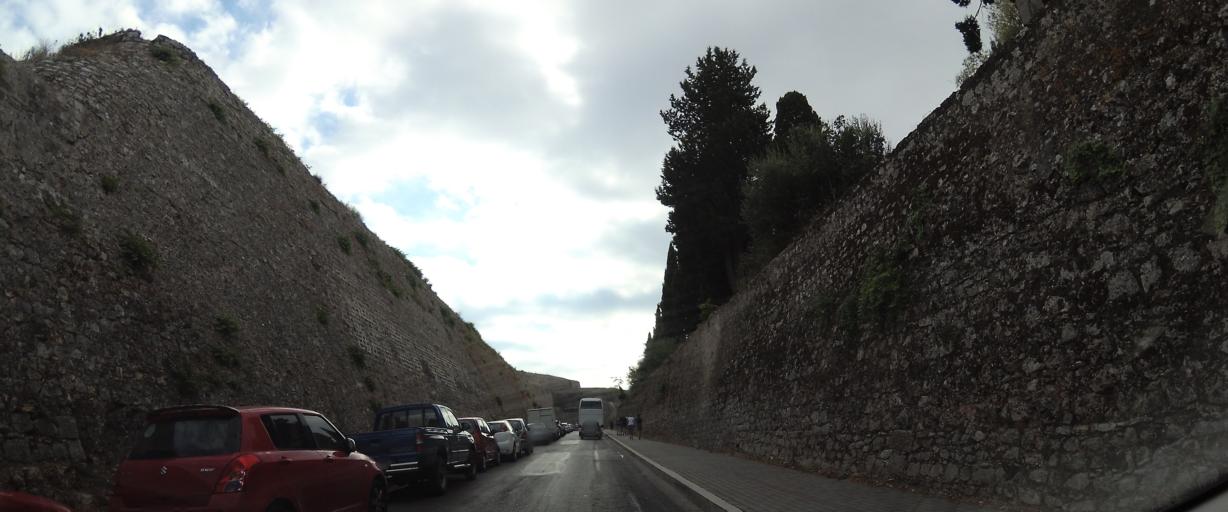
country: GR
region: Ionian Islands
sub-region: Nomos Kerkyras
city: Kerkyra
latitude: 39.6259
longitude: 19.9144
